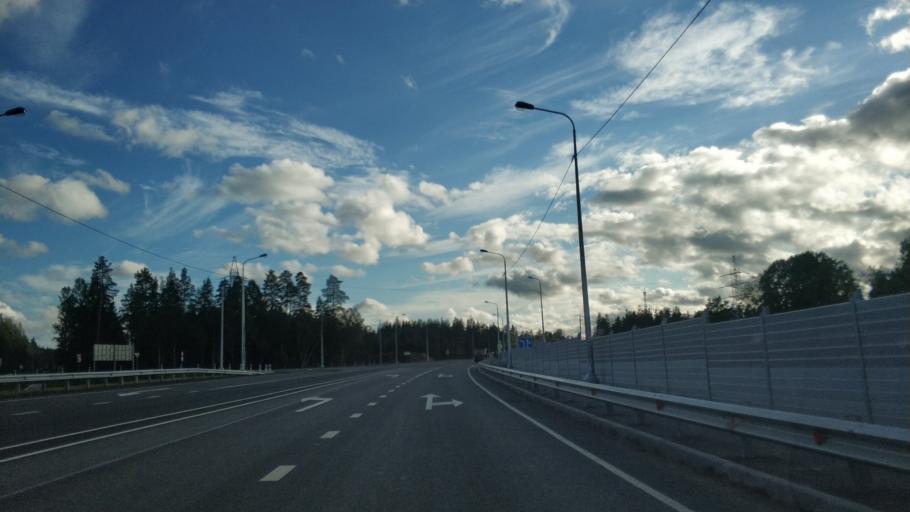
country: RU
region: Leningrad
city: Priozersk
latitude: 60.8486
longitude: 30.1460
